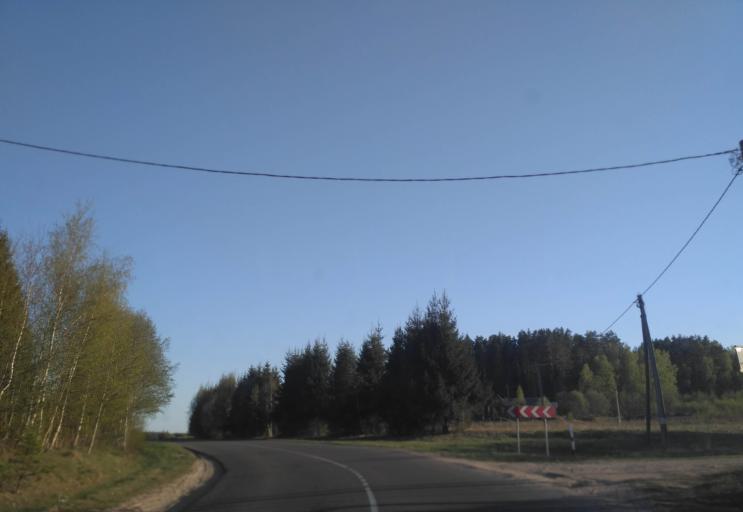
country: BY
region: Minsk
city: Radashkovichy
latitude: 54.1293
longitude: 27.2005
